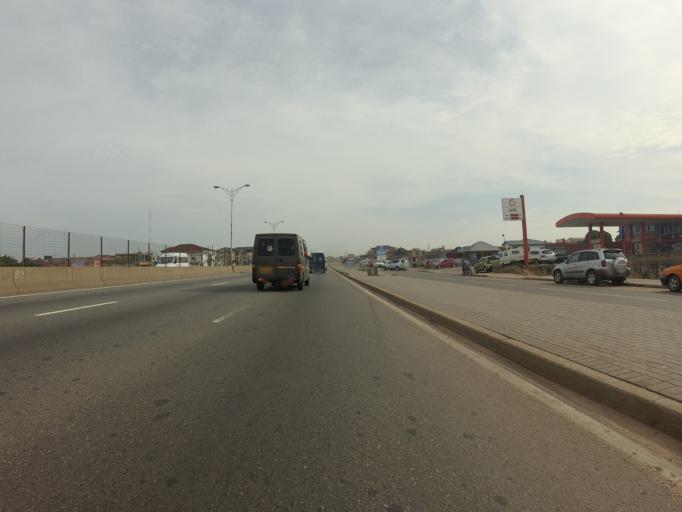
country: GH
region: Greater Accra
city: Gbawe
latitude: 5.5956
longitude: -0.2655
